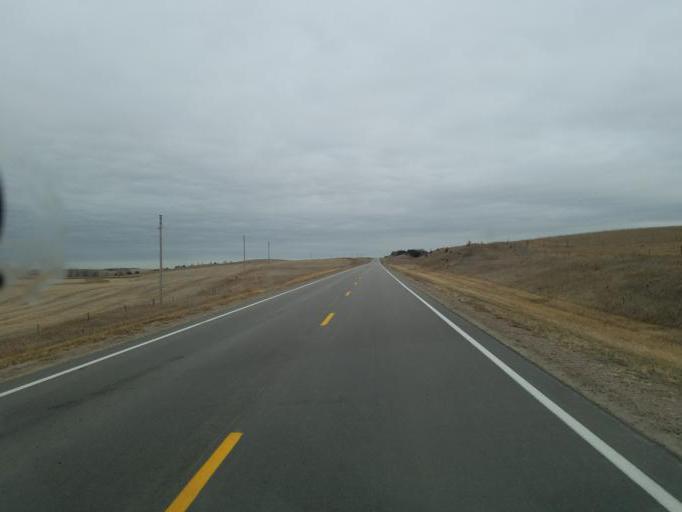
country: US
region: Nebraska
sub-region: Cedar County
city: Hartington
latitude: 42.6128
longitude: -97.3754
